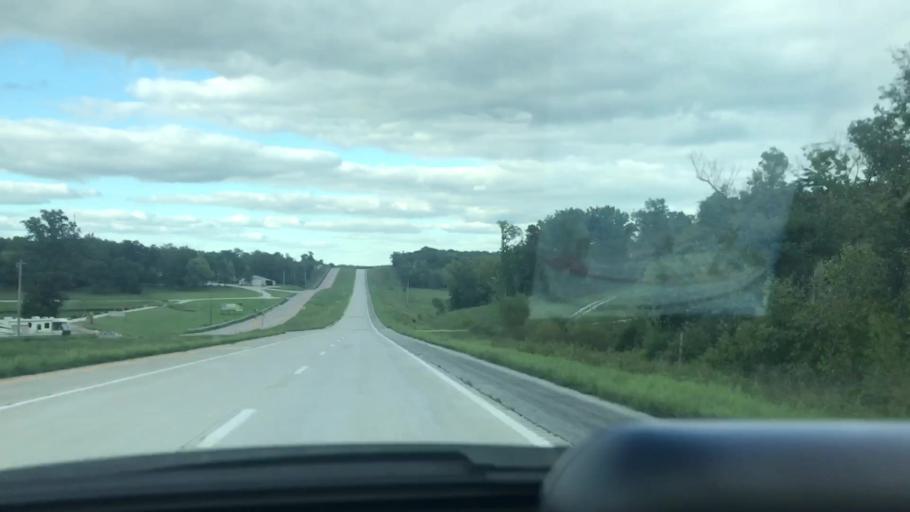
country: US
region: Missouri
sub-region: Benton County
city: Lincoln
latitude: 38.4346
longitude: -93.3035
